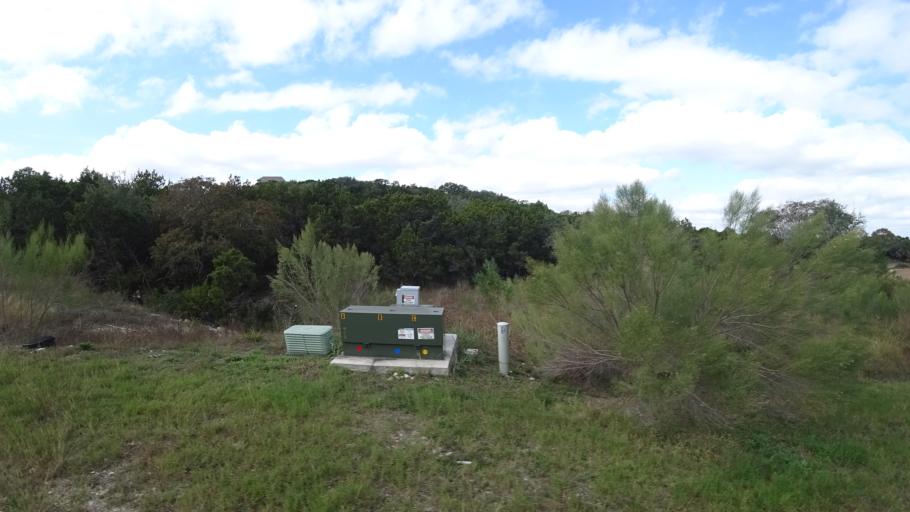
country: US
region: Texas
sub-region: Travis County
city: Bee Cave
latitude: 30.2524
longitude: -97.9273
